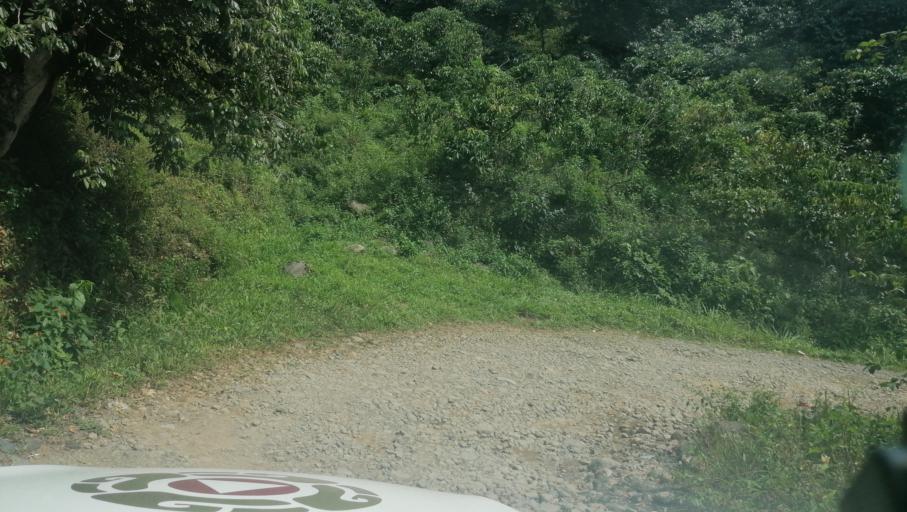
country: MX
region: Chiapas
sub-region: Cacahoatan
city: Benito Juarez
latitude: 15.0401
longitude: -92.2364
